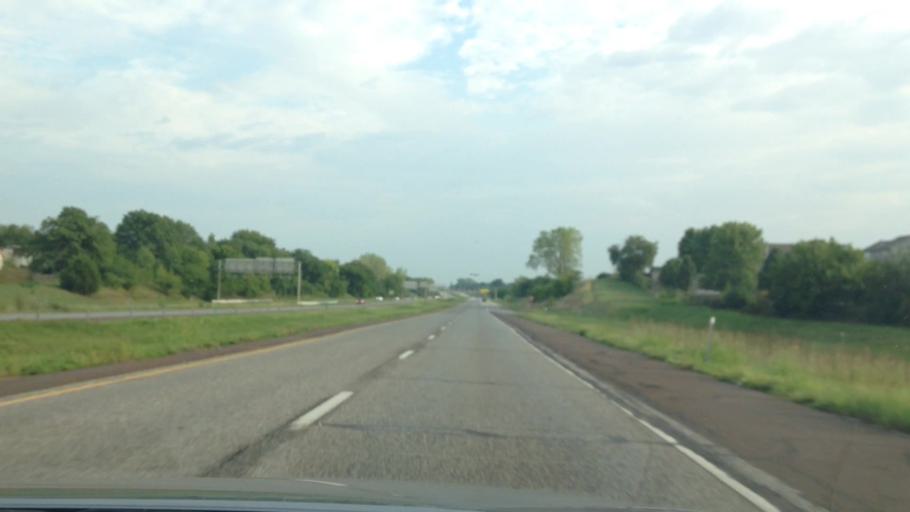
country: US
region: Missouri
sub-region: Clay County
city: Smithville
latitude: 39.3009
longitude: -94.5849
